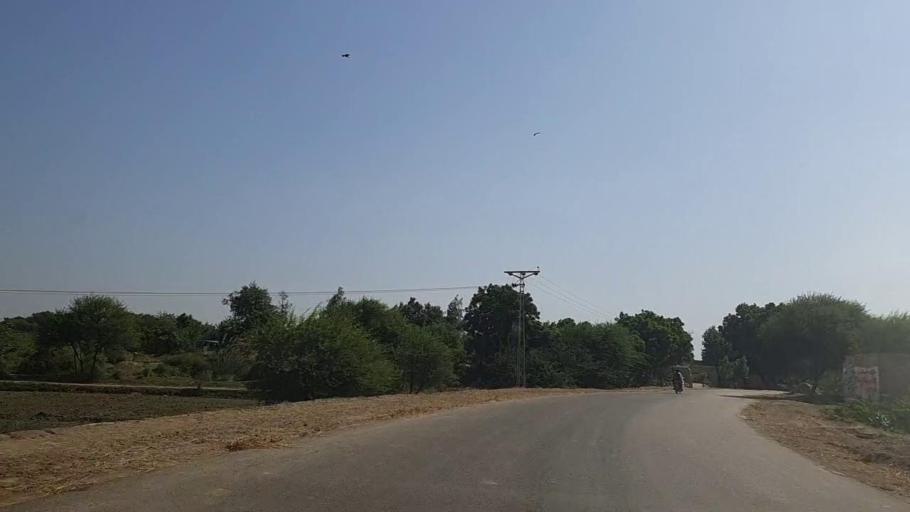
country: PK
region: Sindh
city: Daro Mehar
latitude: 24.7645
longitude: 68.2176
